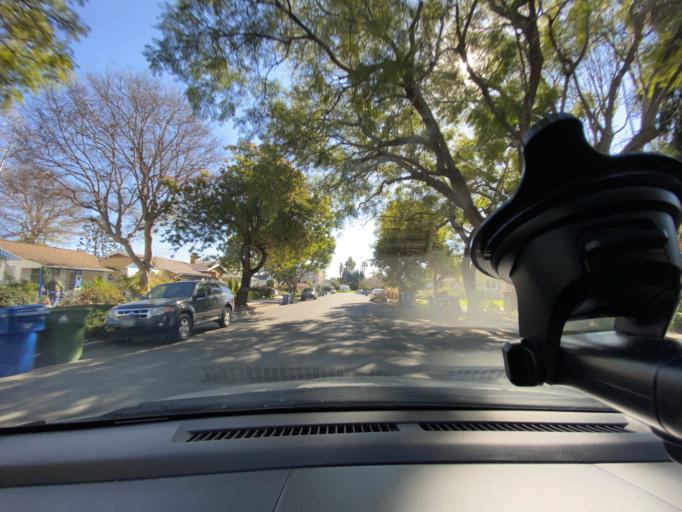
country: US
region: California
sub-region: Los Angeles County
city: Westwood, Los Angeles
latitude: 34.0306
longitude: -118.4258
